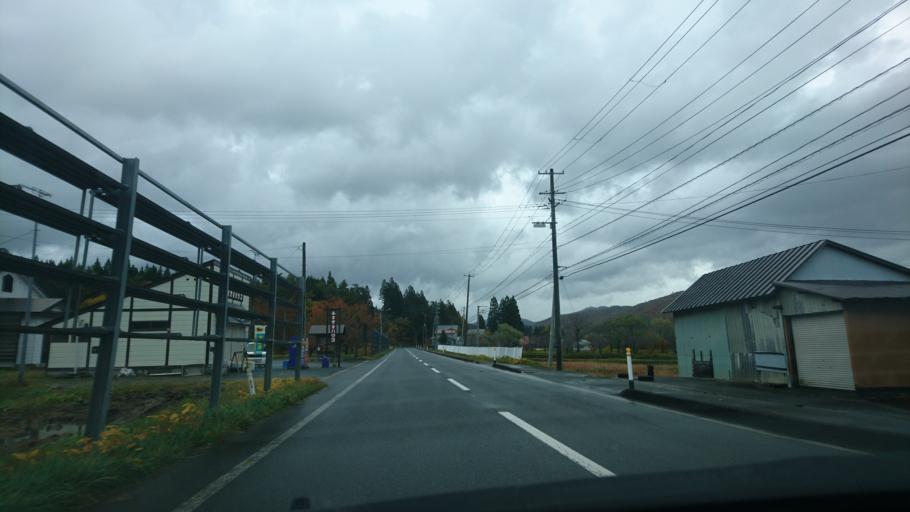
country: JP
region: Akita
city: Kakunodatemachi
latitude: 39.4933
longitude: 140.8127
